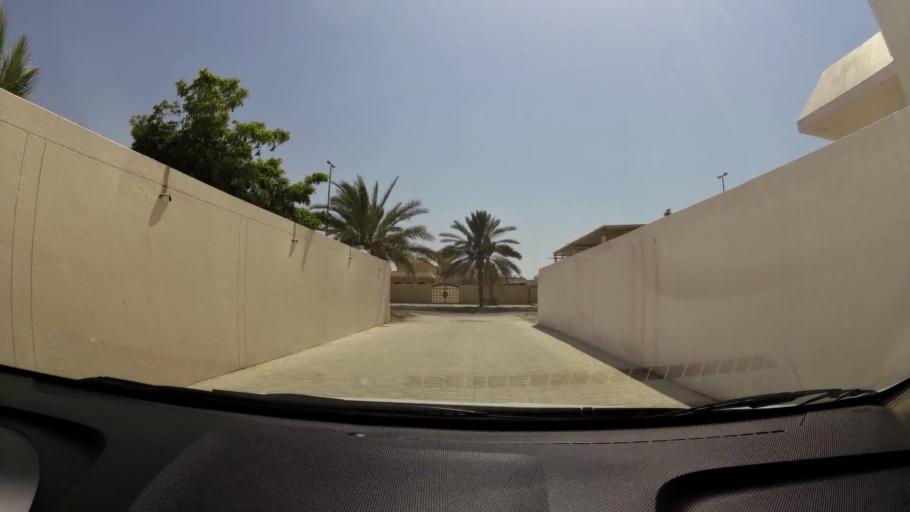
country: AE
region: Ajman
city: Ajman
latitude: 25.4214
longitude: 55.4704
